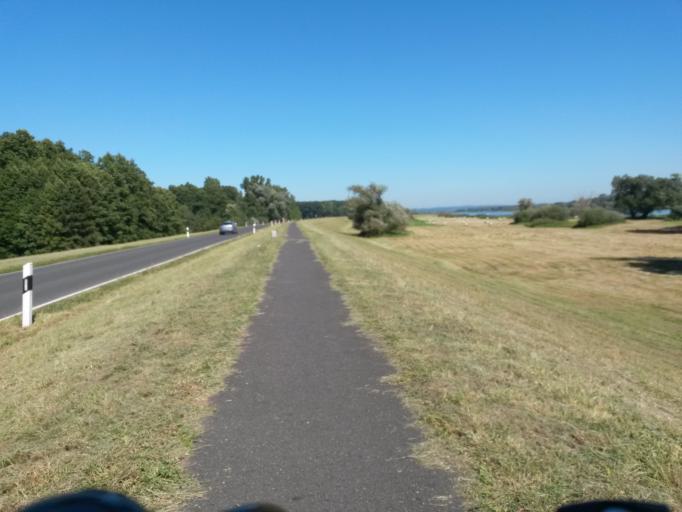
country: PL
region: West Pomeranian Voivodeship
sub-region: Powiat gryfinski
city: Cedynia
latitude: 52.8520
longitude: 14.1258
